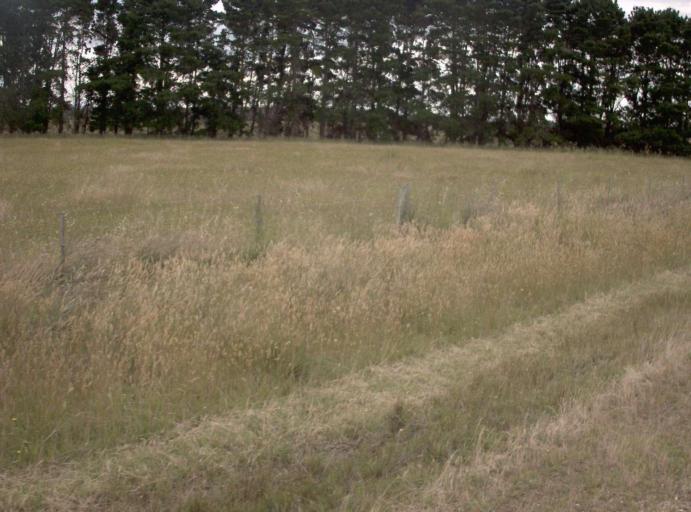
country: AU
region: Victoria
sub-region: East Gippsland
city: Bairnsdale
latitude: -37.9526
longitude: 147.5155
